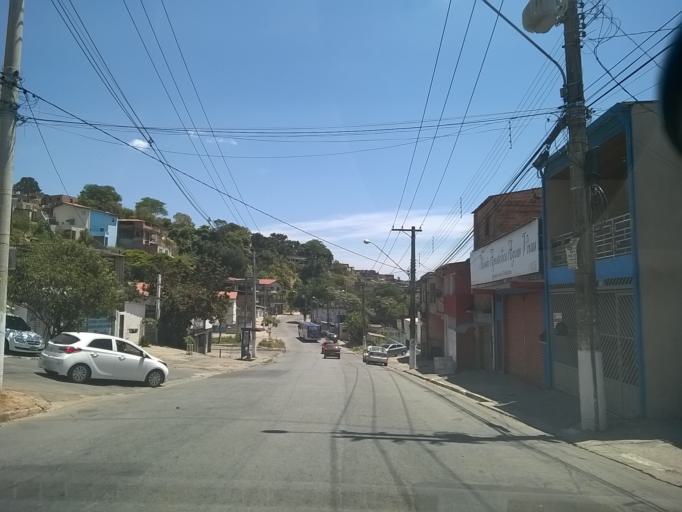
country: BR
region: Sao Paulo
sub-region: Francisco Morato
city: Francisco Morato
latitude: -23.2916
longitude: -46.7399
